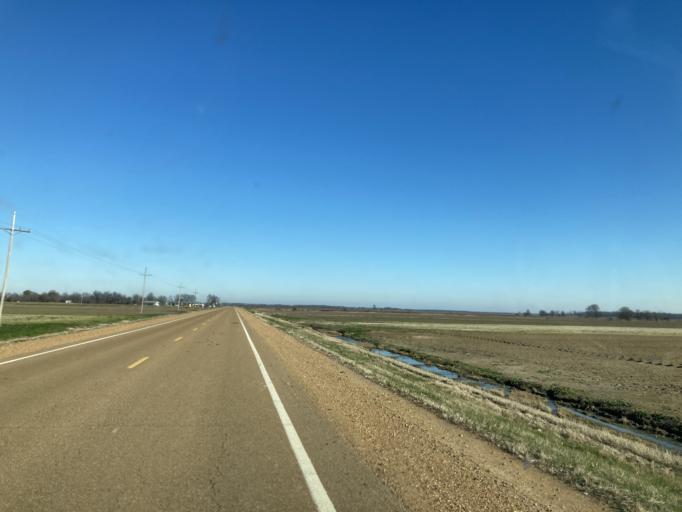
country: US
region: Mississippi
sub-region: Yazoo County
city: Yazoo City
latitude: 32.9528
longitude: -90.5843
